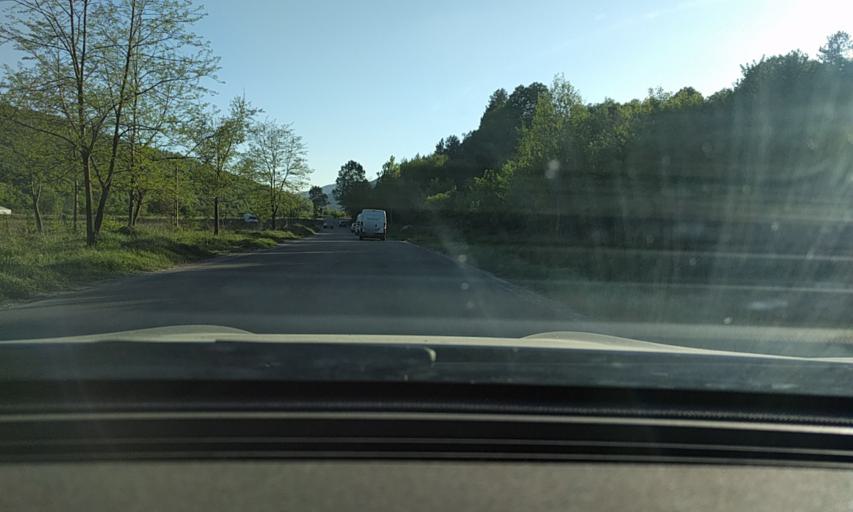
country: RO
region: Bacau
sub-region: Oras Slanic-Moldova
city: Slanic-Moldova
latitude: 46.1863
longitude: 26.4992
